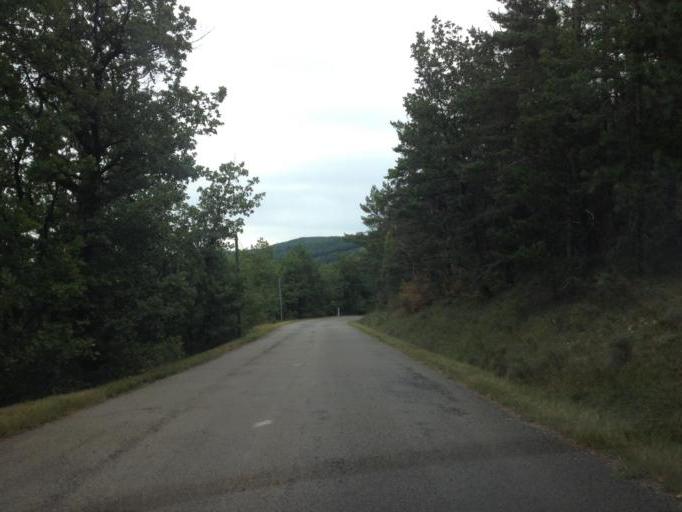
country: FR
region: Rhone-Alpes
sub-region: Departement de la Drome
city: Allan
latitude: 44.4771
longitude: 4.7974
